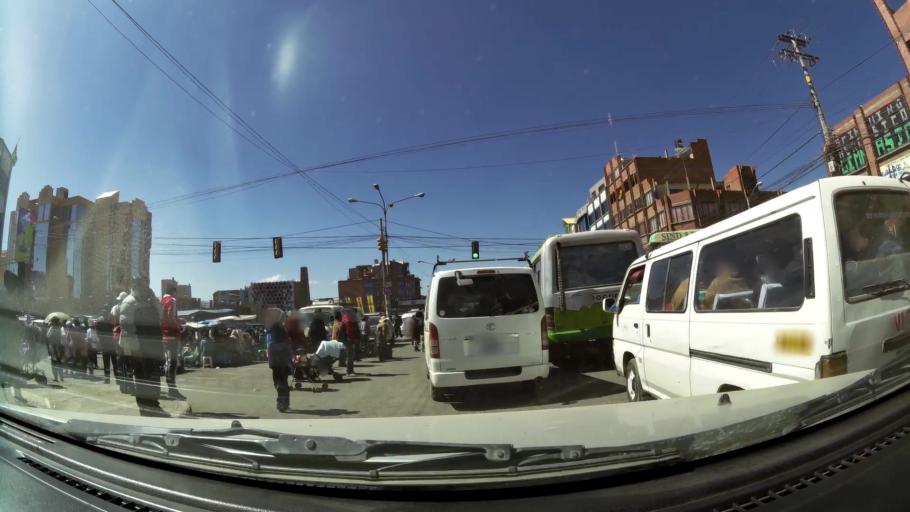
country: BO
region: La Paz
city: La Paz
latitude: -16.4939
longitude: -68.1951
